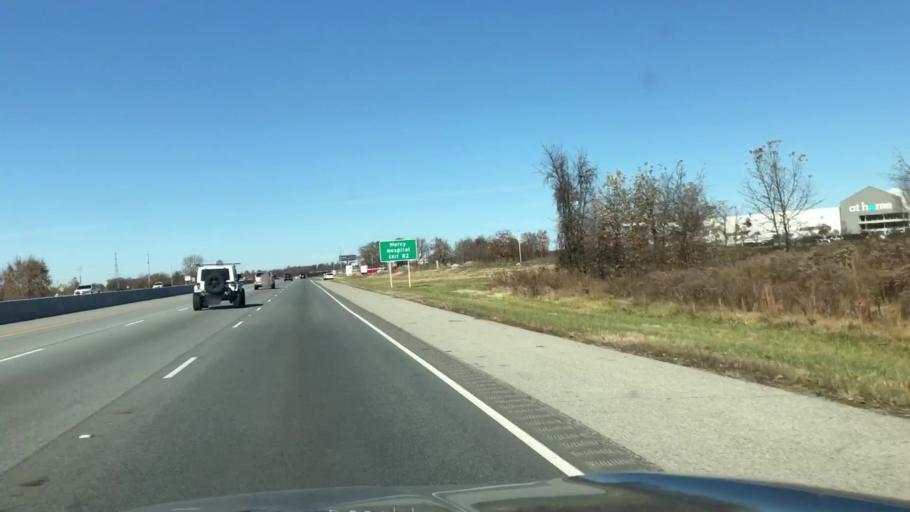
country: US
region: Arkansas
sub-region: Benton County
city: Lowell
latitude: 36.2842
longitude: -94.1570
